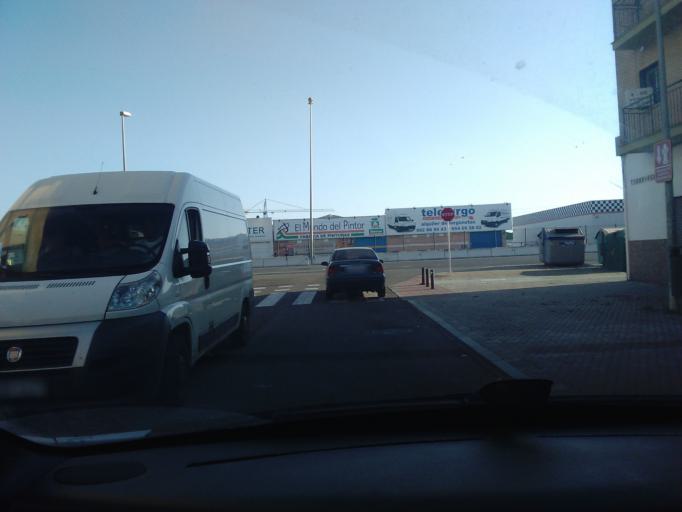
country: ES
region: Andalusia
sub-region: Provincia de Sevilla
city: Sevilla
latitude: 37.3825
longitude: -5.9043
